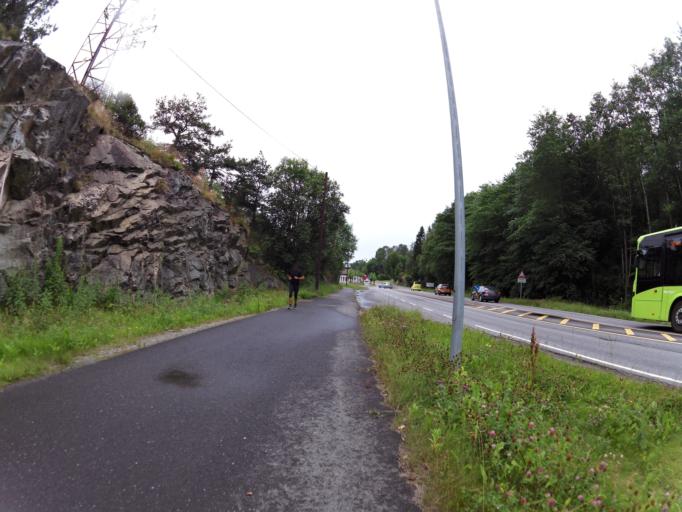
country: NO
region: Ostfold
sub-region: Moss
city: Moss
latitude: 59.4533
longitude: 10.6880
